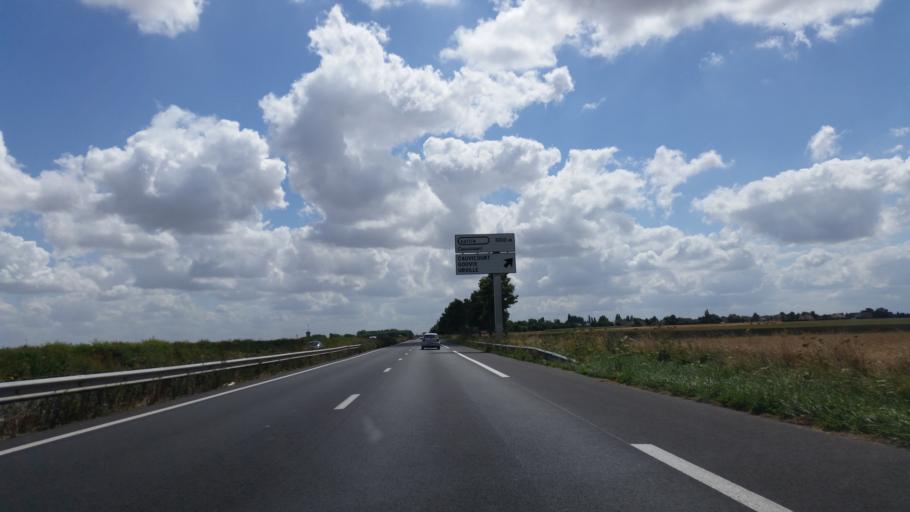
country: FR
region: Lower Normandy
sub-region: Departement du Calvados
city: Bretteville-sur-Laize
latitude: 49.0526
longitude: -0.2856
